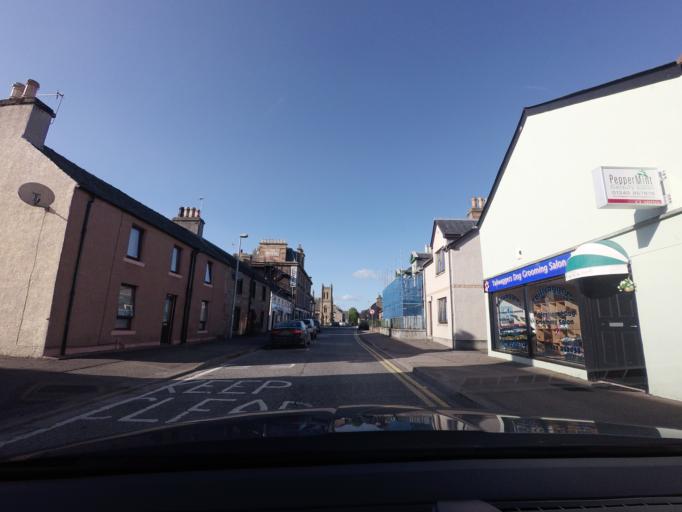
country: GB
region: Scotland
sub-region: Highland
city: Dingwall
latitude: 57.5946
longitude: -4.4259
